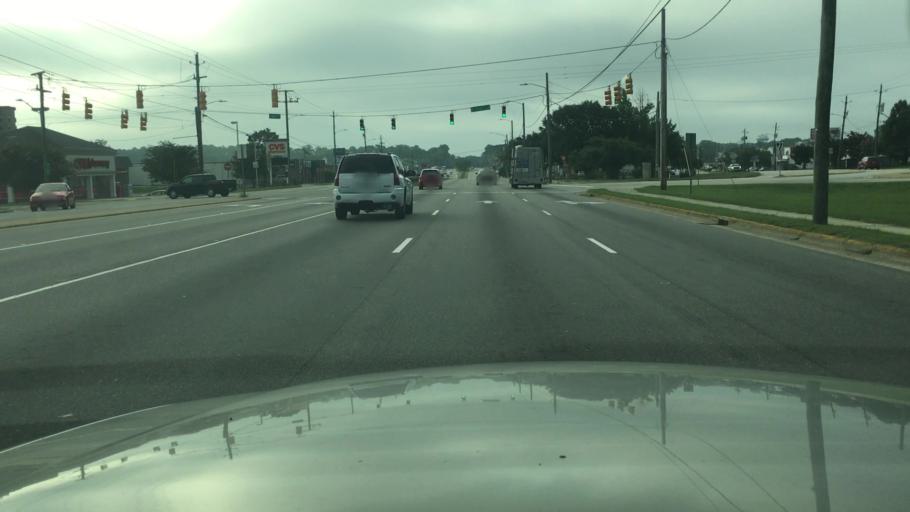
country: US
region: North Carolina
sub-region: Cumberland County
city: Fayetteville
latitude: 35.0752
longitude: -78.9310
